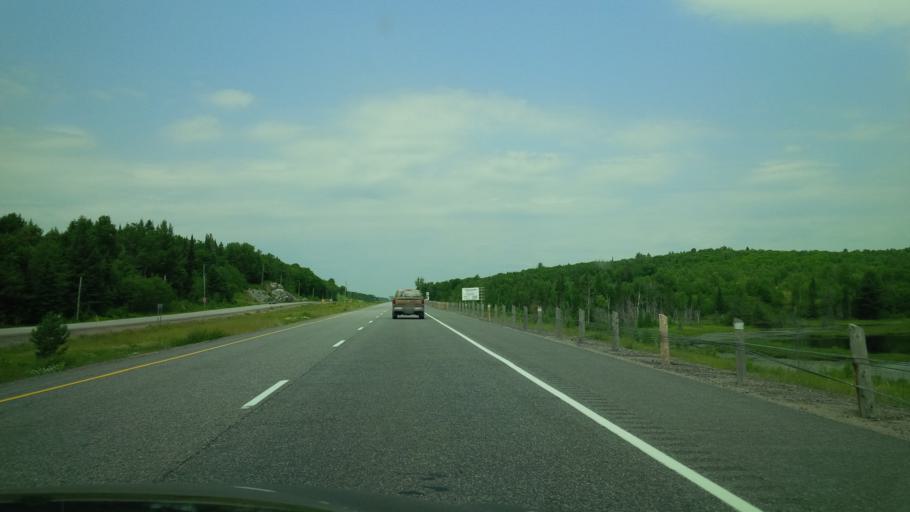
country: CA
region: Ontario
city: Huntsville
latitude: 45.4631
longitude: -79.2597
